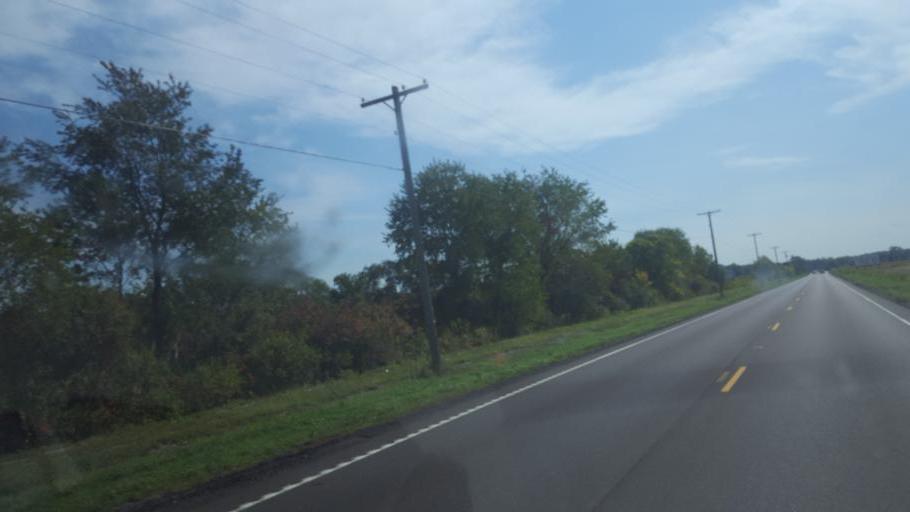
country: US
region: Ohio
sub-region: Knox County
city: Fredericktown
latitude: 40.4379
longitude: -82.5204
